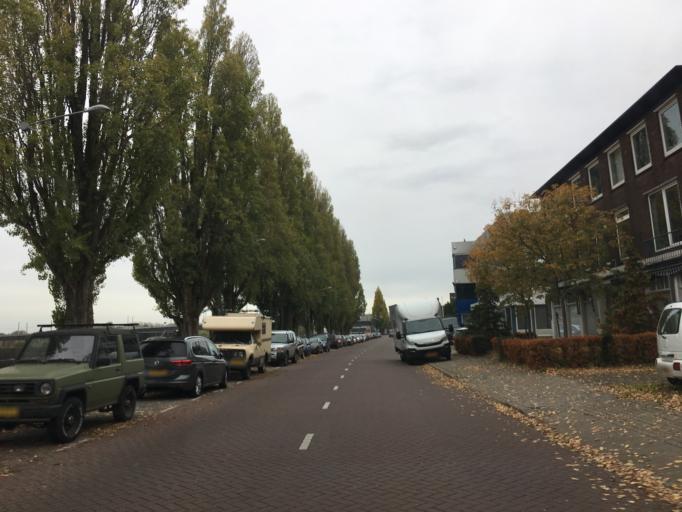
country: NL
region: Gelderland
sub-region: Gemeente Arnhem
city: Arnhem
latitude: 51.9729
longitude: 5.9173
